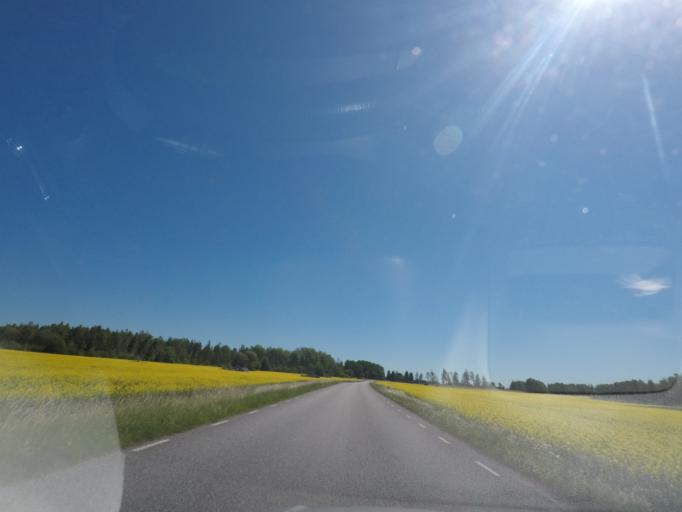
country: SE
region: Uppsala
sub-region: Enkopings Kommun
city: Irsta
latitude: 59.6781
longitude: 16.9266
